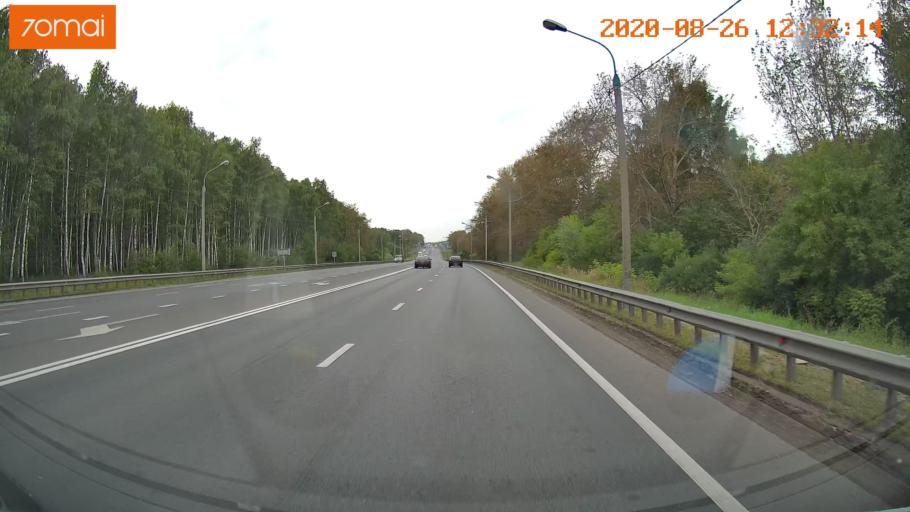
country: RU
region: Rjazan
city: Ryazan'
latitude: 54.5760
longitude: 39.7939
